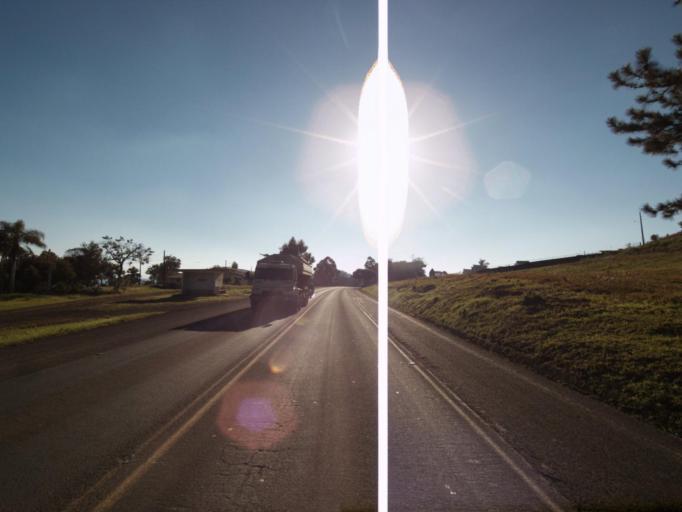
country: BR
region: Santa Catarina
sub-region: Chapeco
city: Chapeco
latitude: -26.9734
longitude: -52.7462
